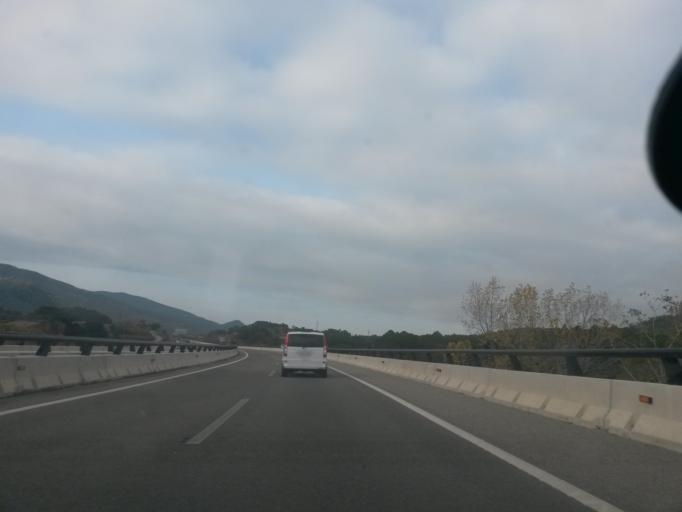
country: ES
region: Catalonia
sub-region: Provincia de Girona
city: Besalu
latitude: 42.2071
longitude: 2.6983
